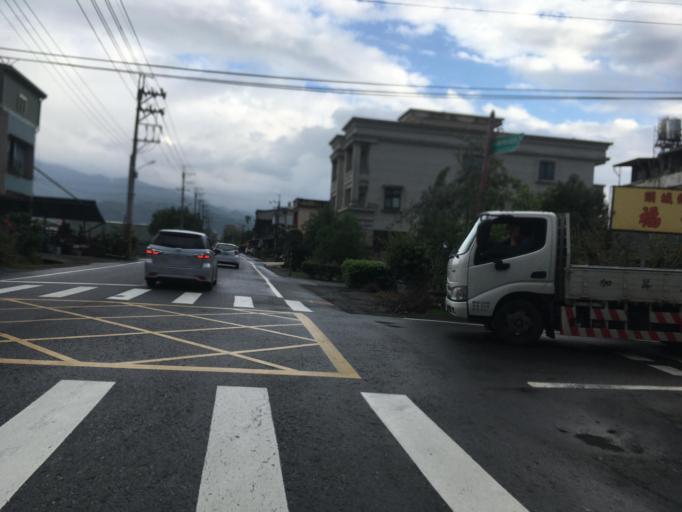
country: TW
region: Taiwan
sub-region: Yilan
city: Yilan
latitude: 24.8384
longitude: 121.8052
